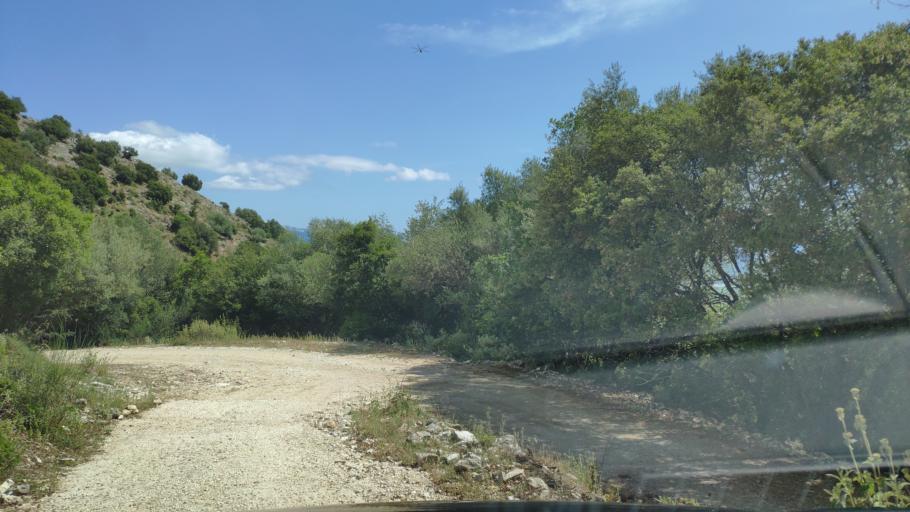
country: AL
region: Vlore
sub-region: Rrethi i Sarandes
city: Konispol
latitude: 39.6359
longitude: 20.2054
